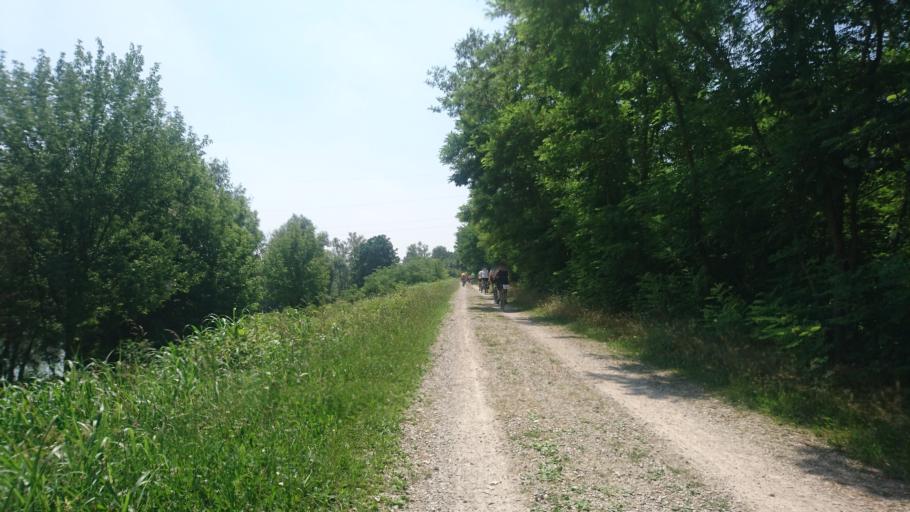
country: IT
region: Veneto
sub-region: Provincia di Venezia
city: Vigonovo
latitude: 45.3936
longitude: 12.0091
